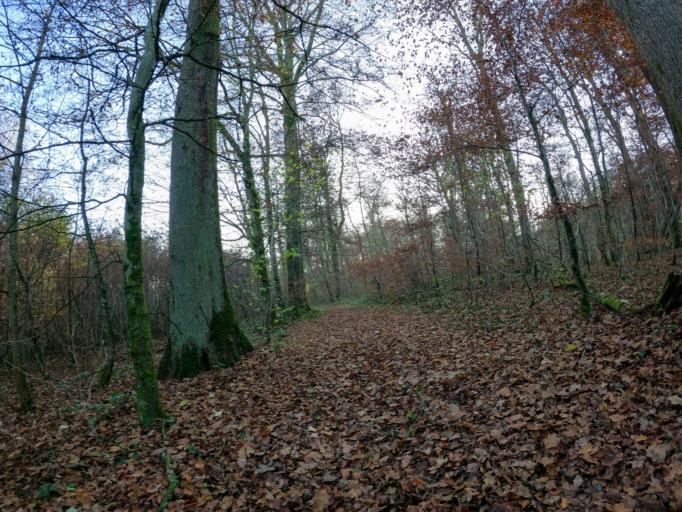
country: LU
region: Luxembourg
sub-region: Canton de Capellen
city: Dippach
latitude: 49.6033
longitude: 6.0063
